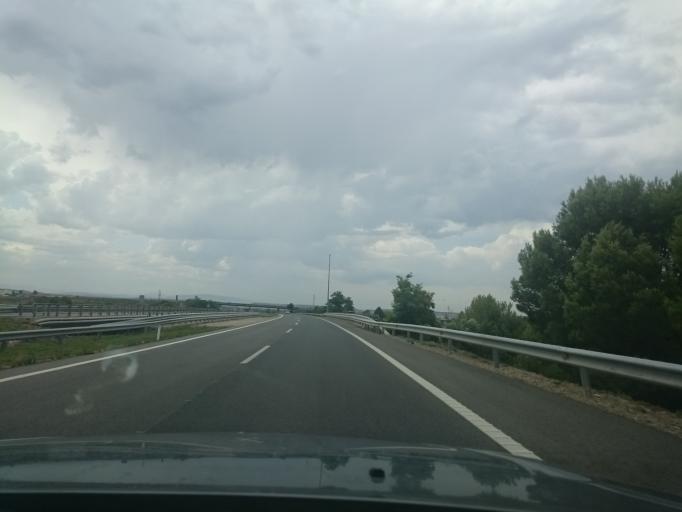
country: ES
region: Navarre
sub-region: Provincia de Navarra
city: Murchante
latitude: 42.0302
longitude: -1.6312
